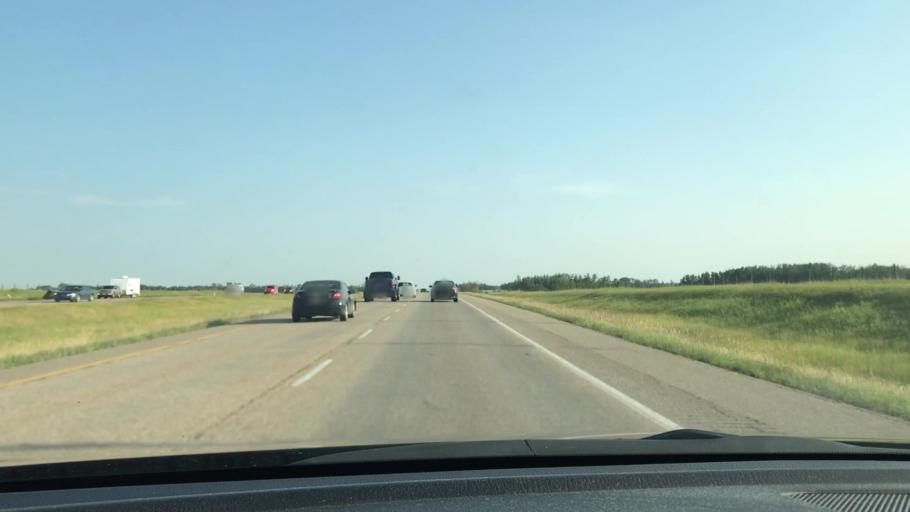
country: CA
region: Alberta
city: Millet
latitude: 53.1254
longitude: -113.5989
